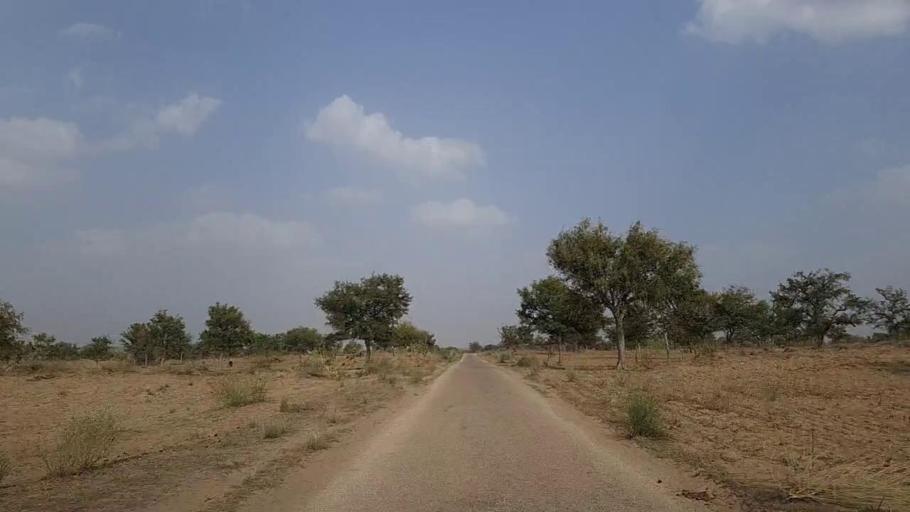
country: PK
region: Sindh
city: Islamkot
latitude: 24.8742
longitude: 70.1438
